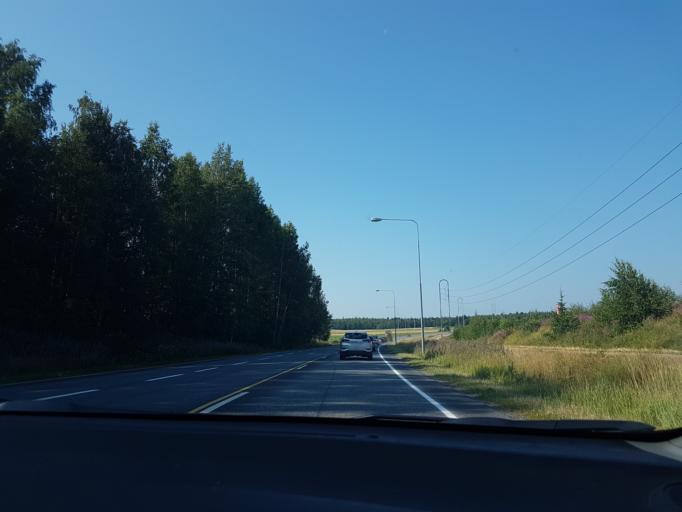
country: FI
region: Uusimaa
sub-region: Helsinki
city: Tuusula
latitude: 60.3763
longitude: 25.0523
